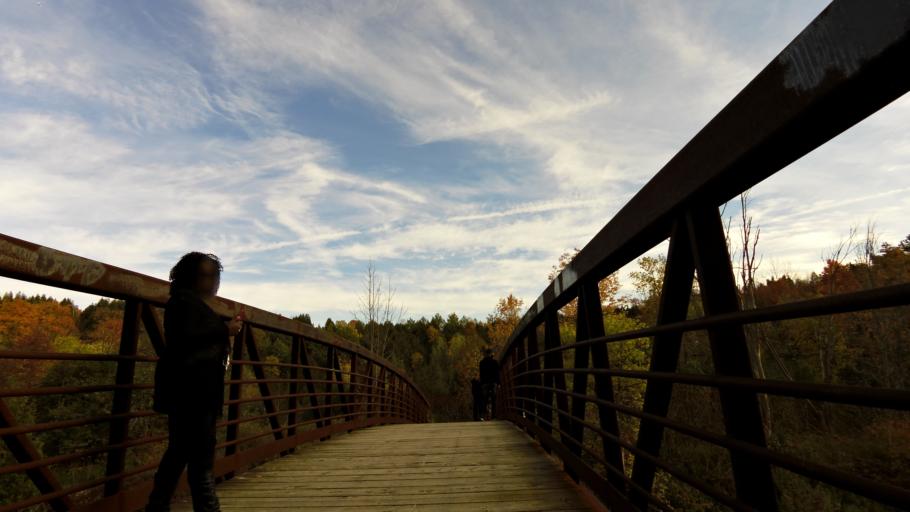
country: CA
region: Ontario
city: Orangeville
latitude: 43.8226
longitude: -80.0210
